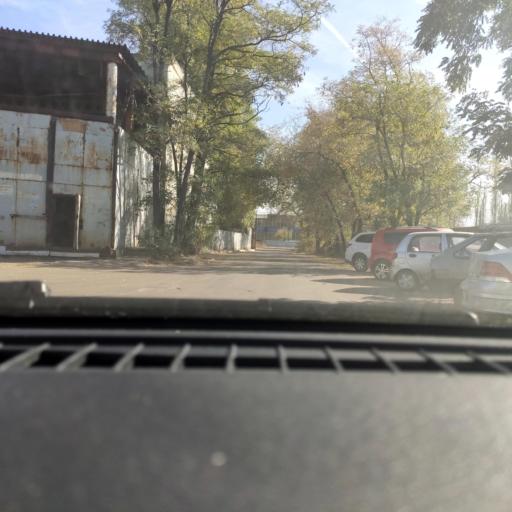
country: RU
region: Voronezj
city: Voronezh
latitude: 51.6525
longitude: 39.2881
